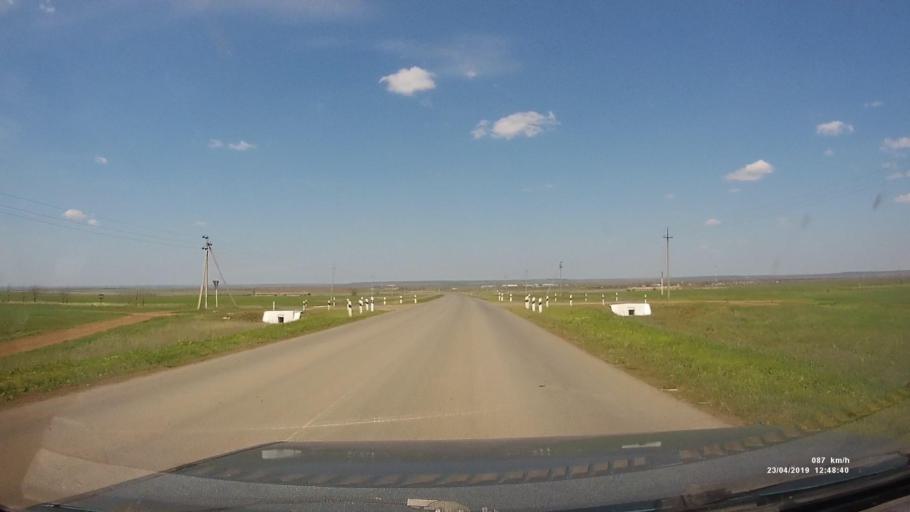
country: RU
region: Kalmykiya
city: Yashalta
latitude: 46.5272
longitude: 42.6389
